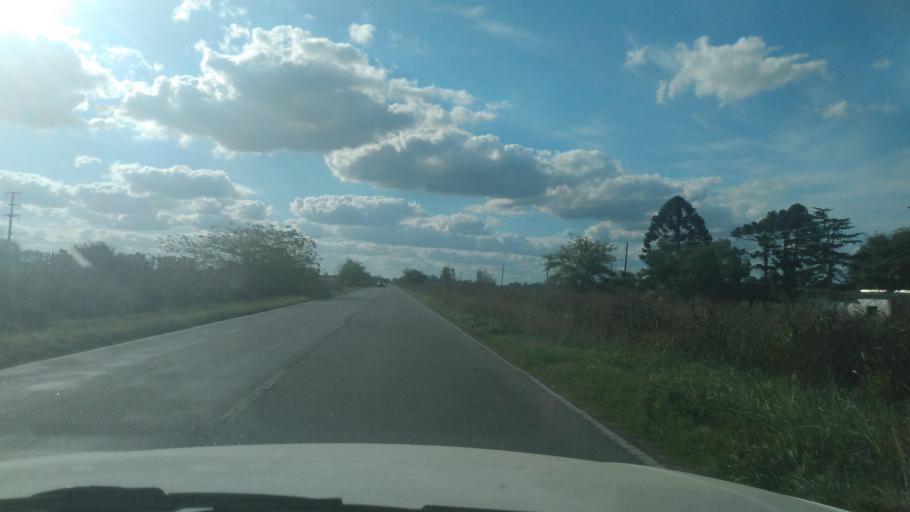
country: AR
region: Buenos Aires
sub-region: Partido de Mercedes
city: Mercedes
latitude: -34.7408
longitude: -59.3853
